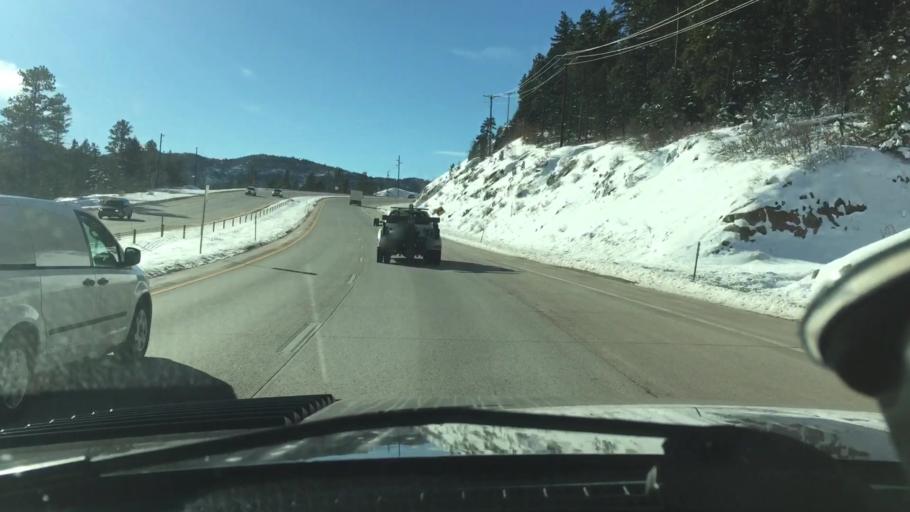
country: US
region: Colorado
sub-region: Jefferson County
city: Indian Hills
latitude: 39.5603
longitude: -105.2398
